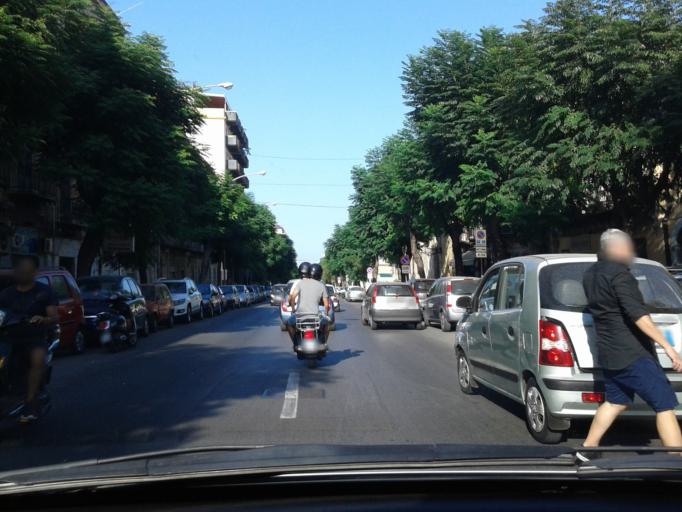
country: IT
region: Sicily
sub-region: Palermo
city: Palermo
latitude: 38.1079
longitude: 13.3421
